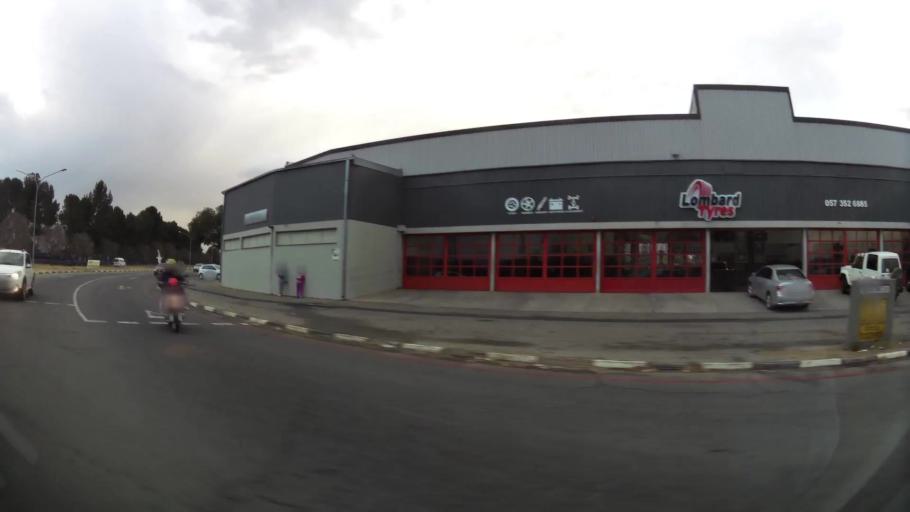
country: ZA
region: Orange Free State
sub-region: Lejweleputswa District Municipality
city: Welkom
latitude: -27.9692
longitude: 26.7487
